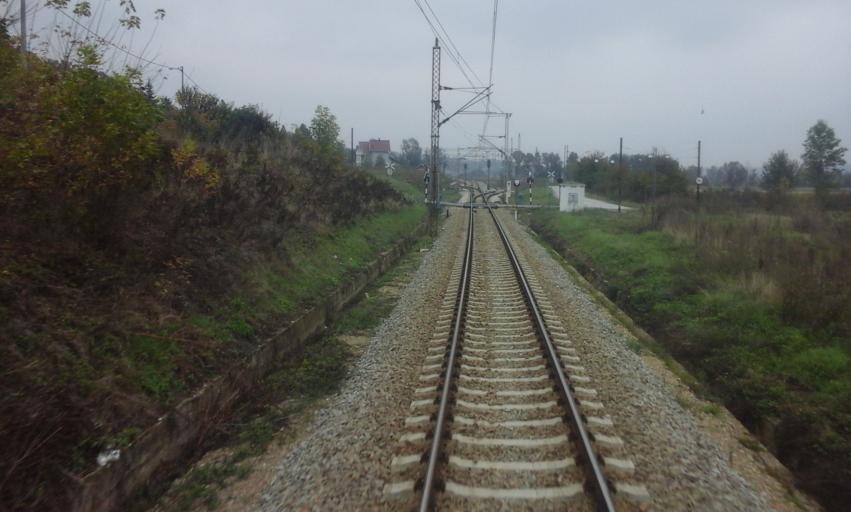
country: RS
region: Central Serbia
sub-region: Belgrade
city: Mladenovac
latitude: 44.4856
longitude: 20.6567
